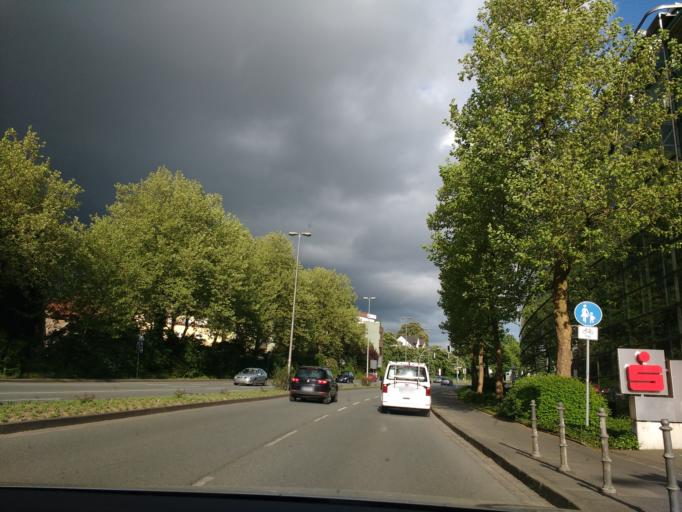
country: DE
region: North Rhine-Westphalia
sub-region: Regierungsbezirk Detmold
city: Bad Salzuflen
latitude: 52.0813
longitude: 8.7481
